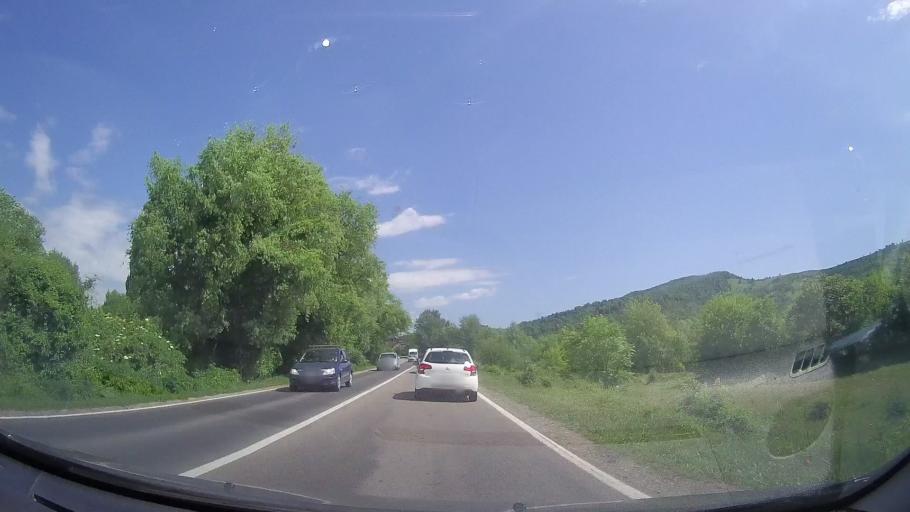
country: RO
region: Prahova
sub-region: Comuna Gura Vitioarei
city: Fagetu
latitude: 45.1337
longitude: 26.0303
